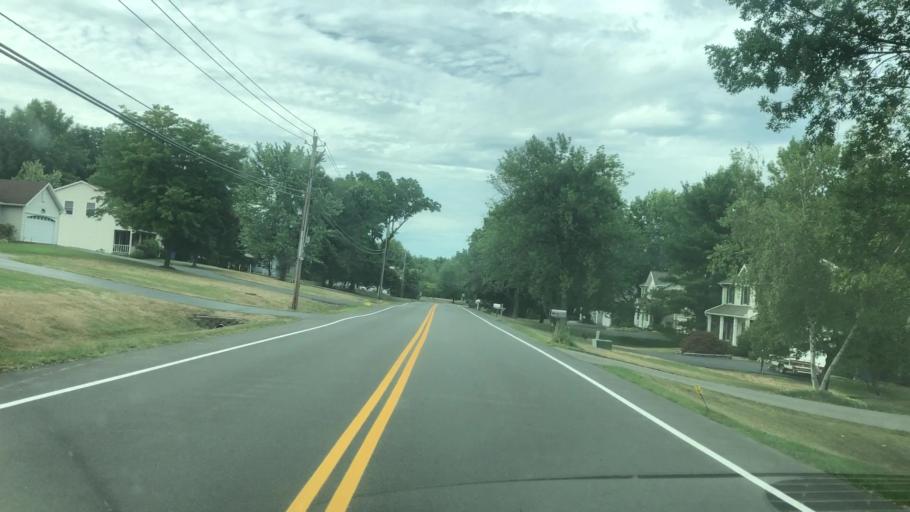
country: US
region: New York
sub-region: Wayne County
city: Macedon
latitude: 43.1296
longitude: -77.3534
